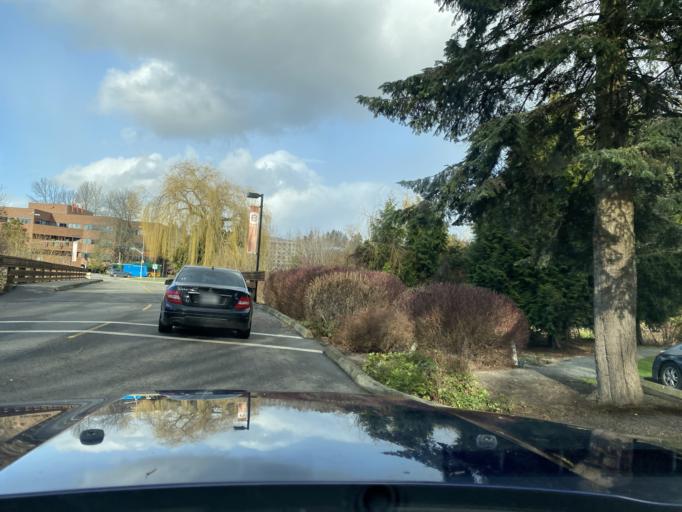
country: US
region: Washington
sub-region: King County
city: Bellevue
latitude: 47.6004
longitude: -122.1878
